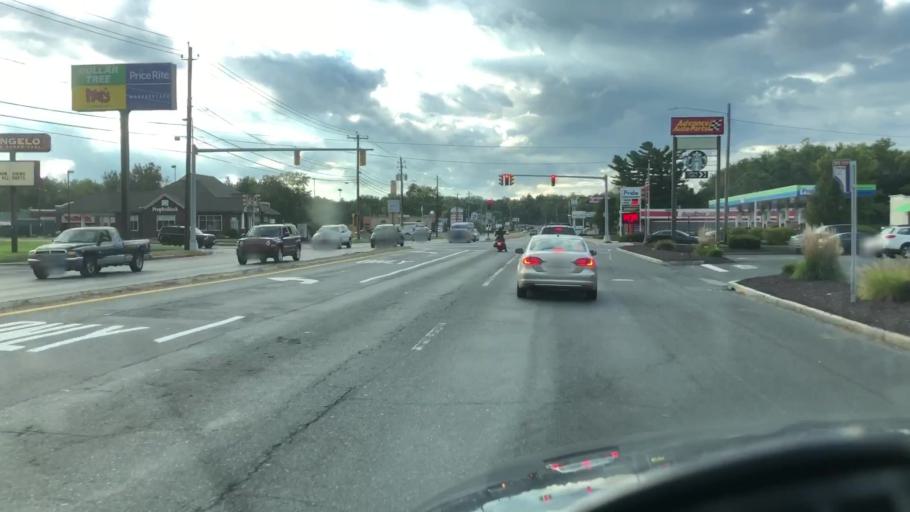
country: US
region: Massachusetts
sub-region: Hampden County
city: Westfield
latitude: 42.1143
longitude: -72.7275
